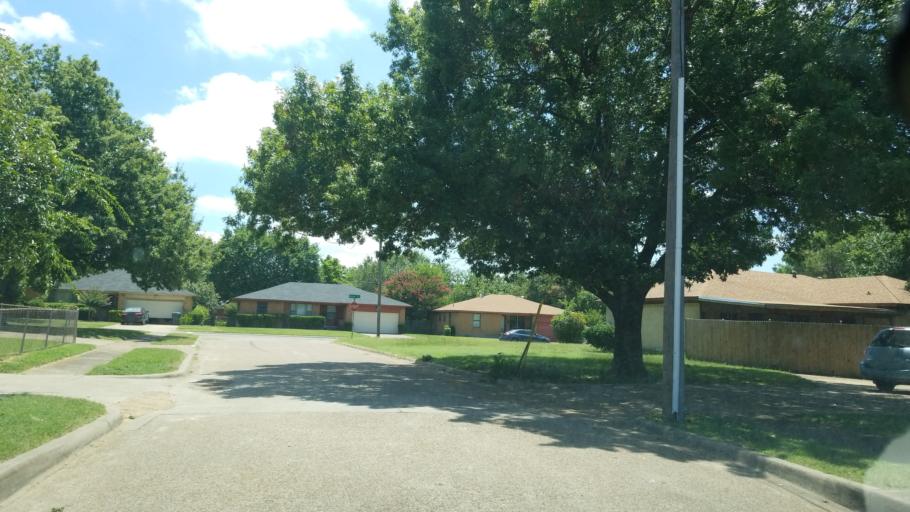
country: US
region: Texas
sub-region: Dallas County
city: Balch Springs
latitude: 32.7397
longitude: -96.7050
